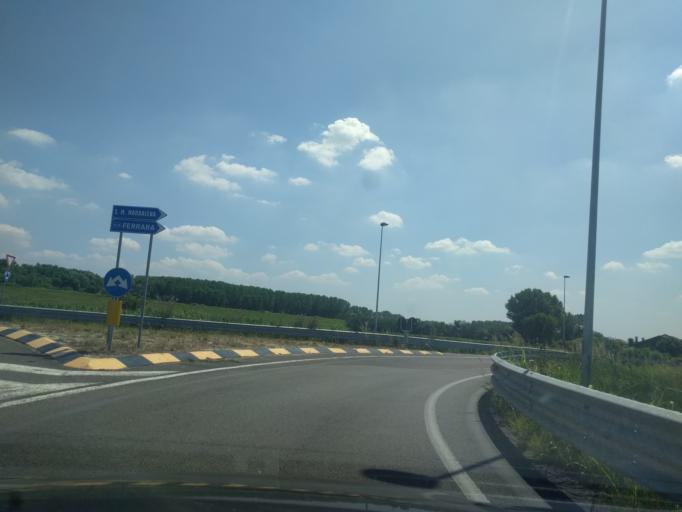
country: IT
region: Veneto
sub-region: Provincia di Rovigo
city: Santa Maria Maddalena
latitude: 44.8989
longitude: 11.6312
